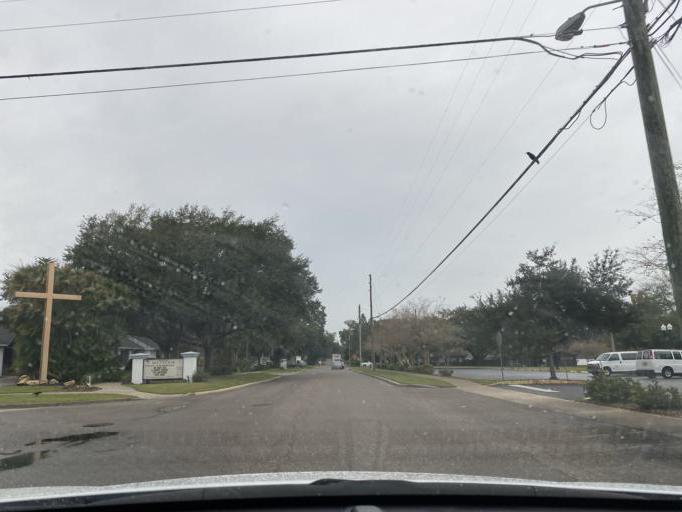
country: US
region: Florida
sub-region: Orange County
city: Winter Garden
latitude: 28.5694
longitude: -81.5845
